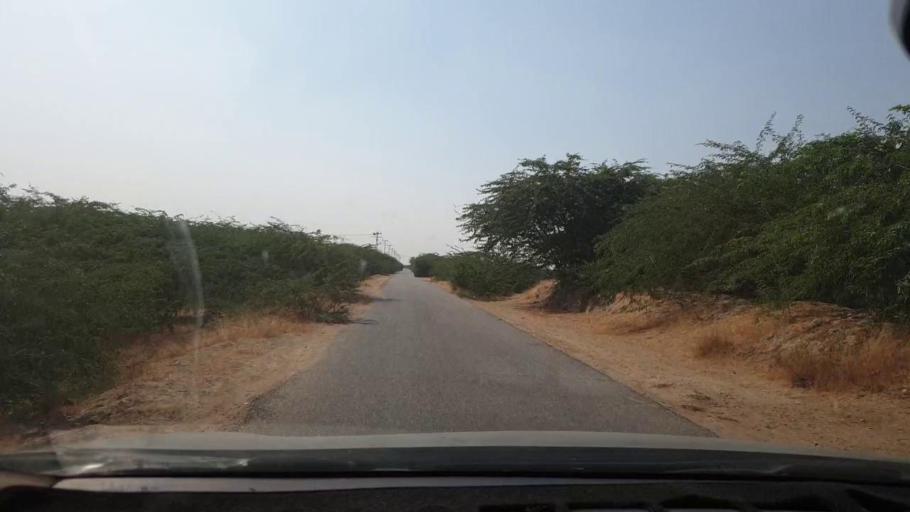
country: PK
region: Sindh
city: Malir Cantonment
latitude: 25.1163
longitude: 67.2114
